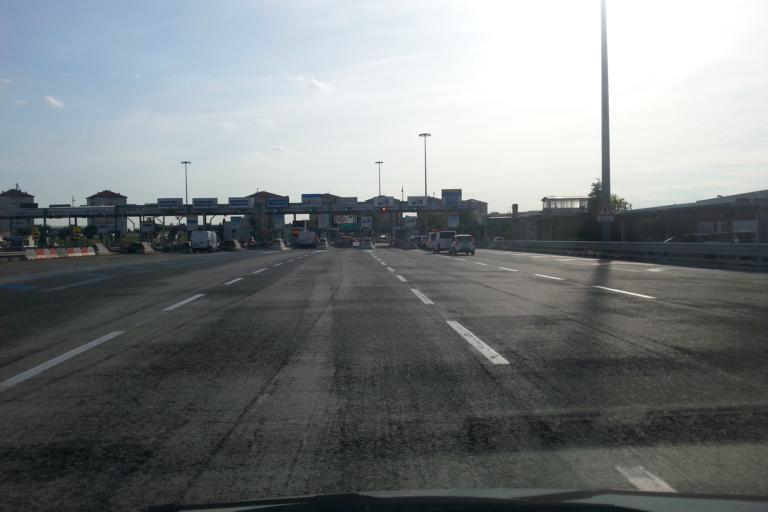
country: IT
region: Piedmont
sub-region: Provincia di Torino
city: Settimo Torinese
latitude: 45.1355
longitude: 7.7169
